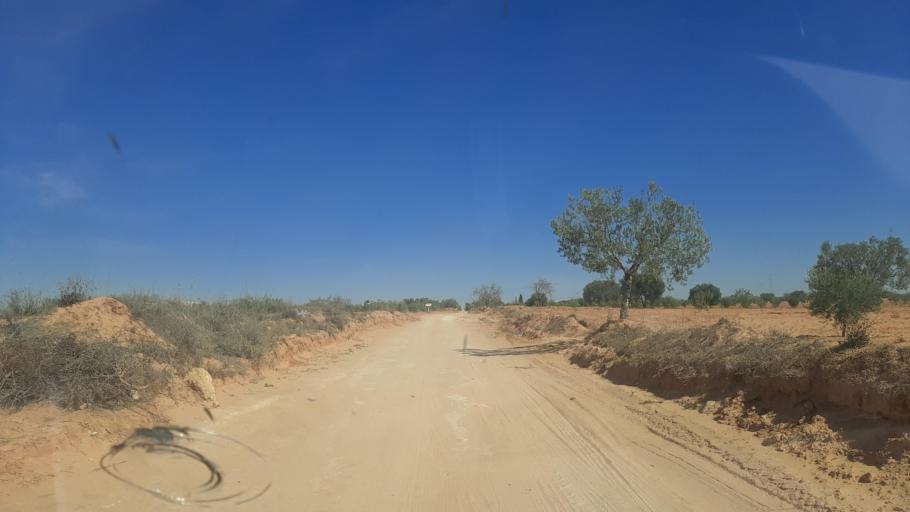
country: TN
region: Safaqis
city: Sfax
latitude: 34.8748
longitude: 10.5666
